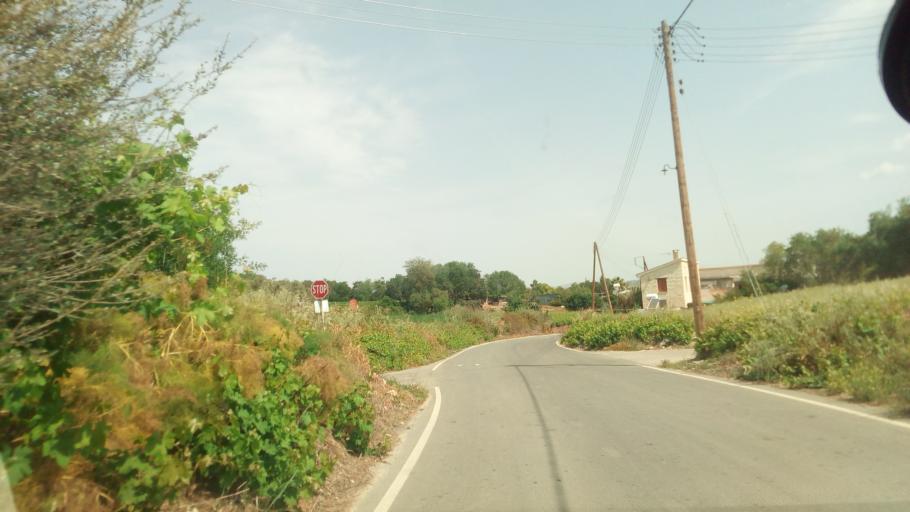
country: CY
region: Pafos
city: Mesogi
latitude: 34.8797
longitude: 32.5048
